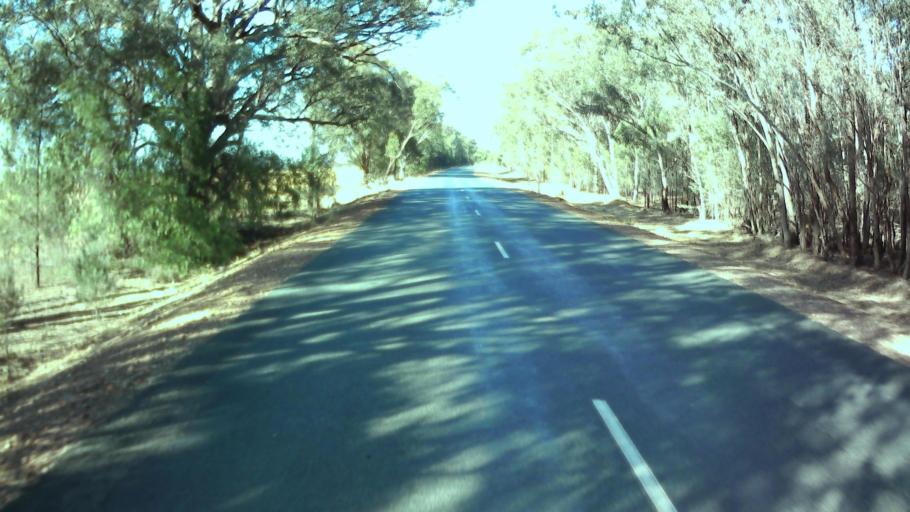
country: AU
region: New South Wales
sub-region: Weddin
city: Grenfell
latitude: -34.0115
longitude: 148.1171
